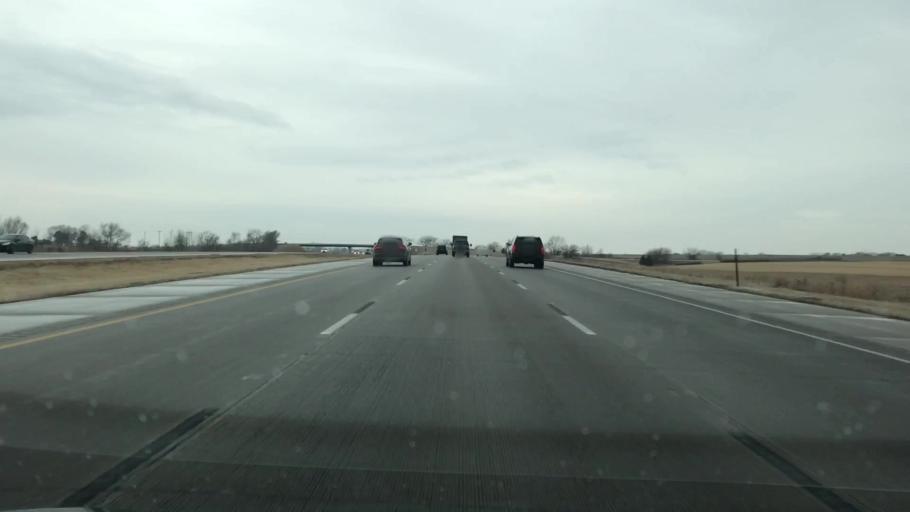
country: US
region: Nebraska
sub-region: Sarpy County
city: Gretna
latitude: 41.1210
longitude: -96.2097
